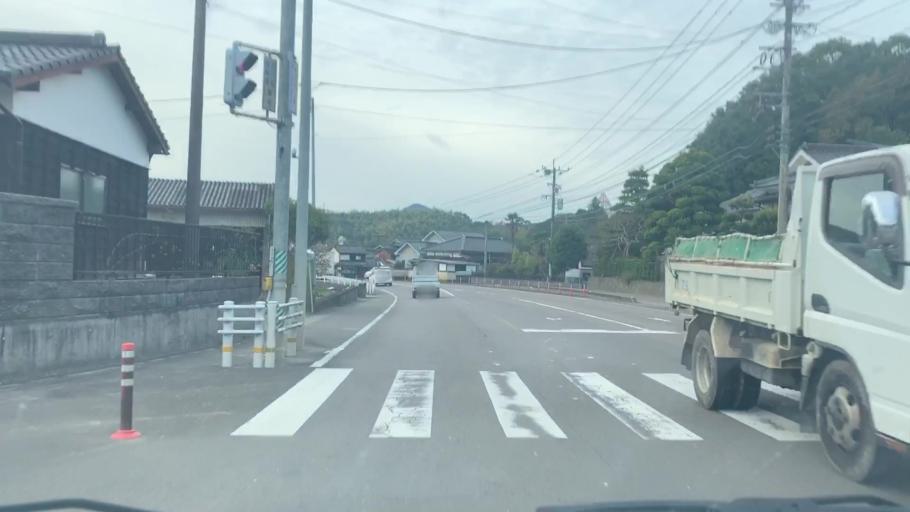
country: JP
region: Saga Prefecture
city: Kashima
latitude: 33.1497
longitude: 130.0635
